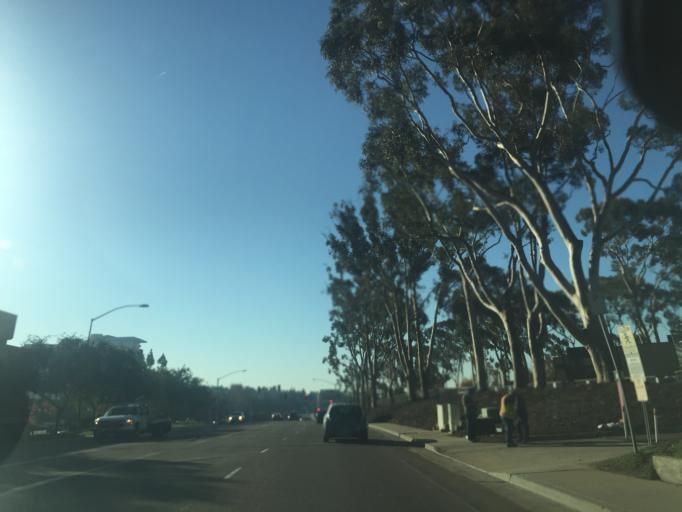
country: US
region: California
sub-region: San Diego County
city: La Jolla
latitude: 32.8739
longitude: -117.2184
